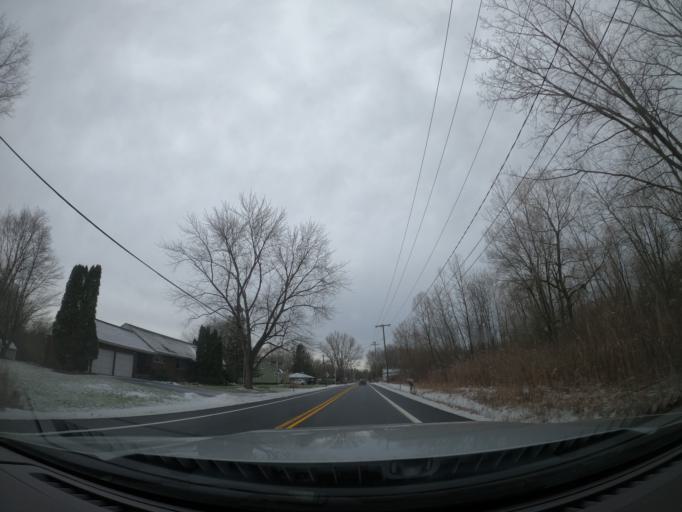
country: US
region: New York
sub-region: Madison County
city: Bridgeport
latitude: 43.1476
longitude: -75.9759
